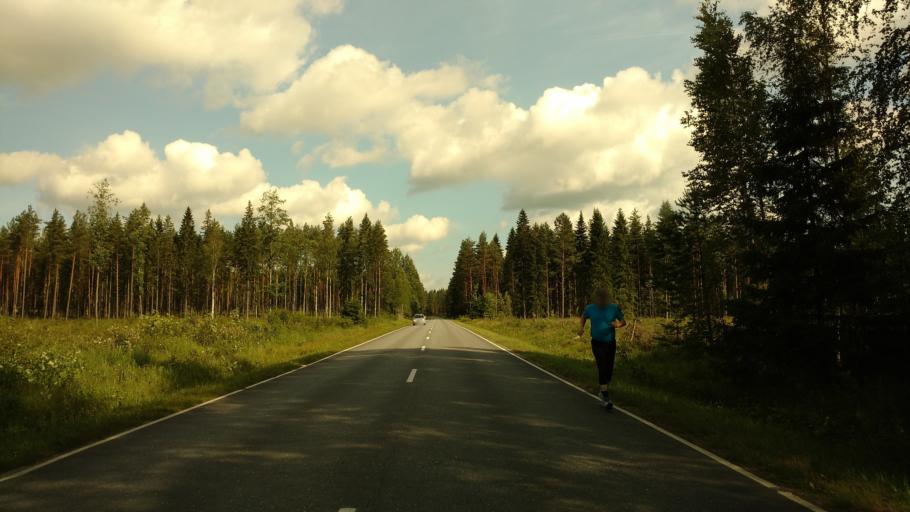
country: FI
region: Varsinais-Suomi
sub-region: Loimaa
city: Koski Tl
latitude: 60.6082
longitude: 23.1217
